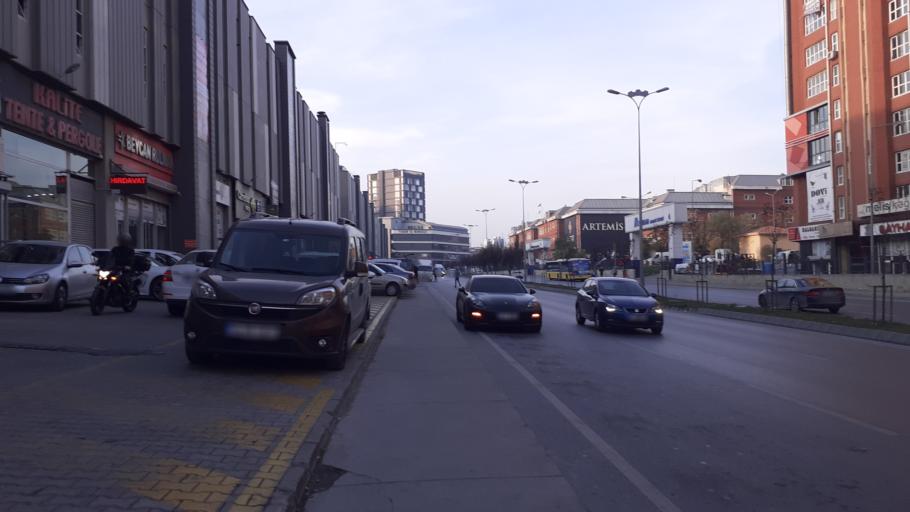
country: TR
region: Istanbul
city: Basaksehir
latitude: 41.0705
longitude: 28.7955
